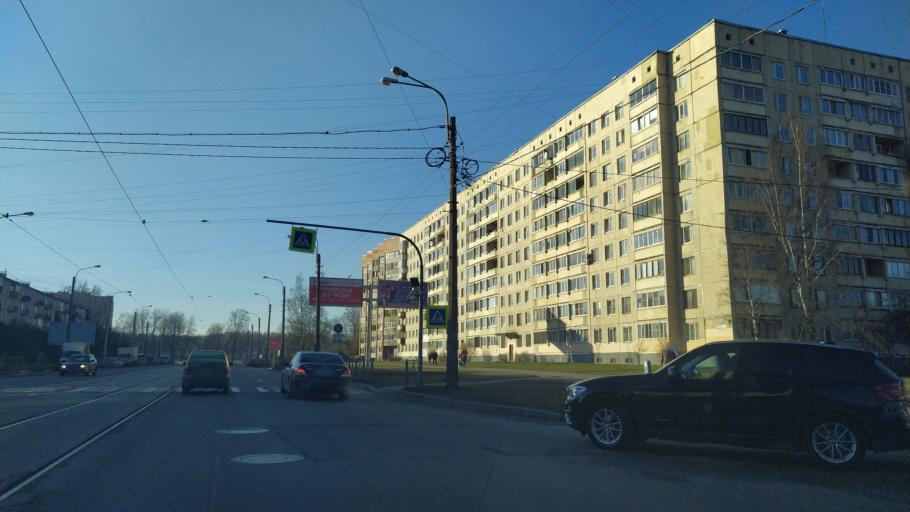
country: RU
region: Leningrad
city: Akademicheskoe
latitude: 60.0166
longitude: 30.3782
